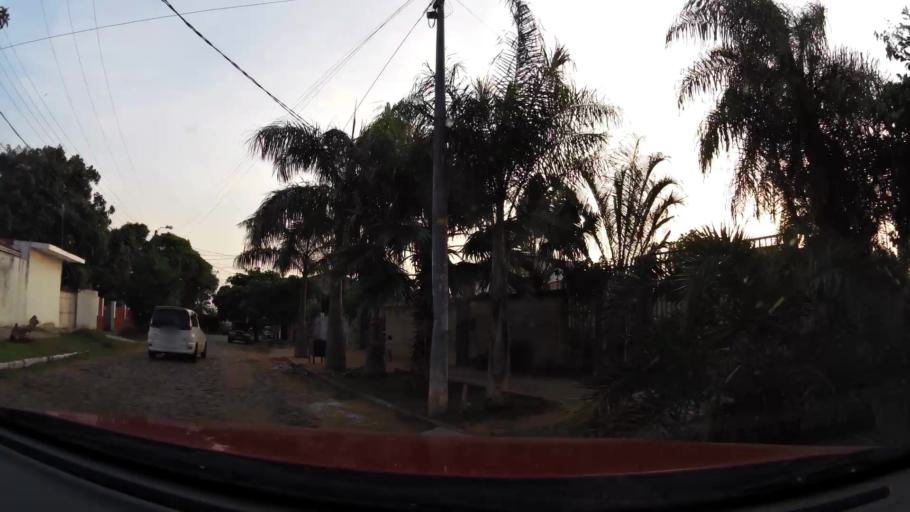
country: PY
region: Central
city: Lambare
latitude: -25.3576
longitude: -57.6031
